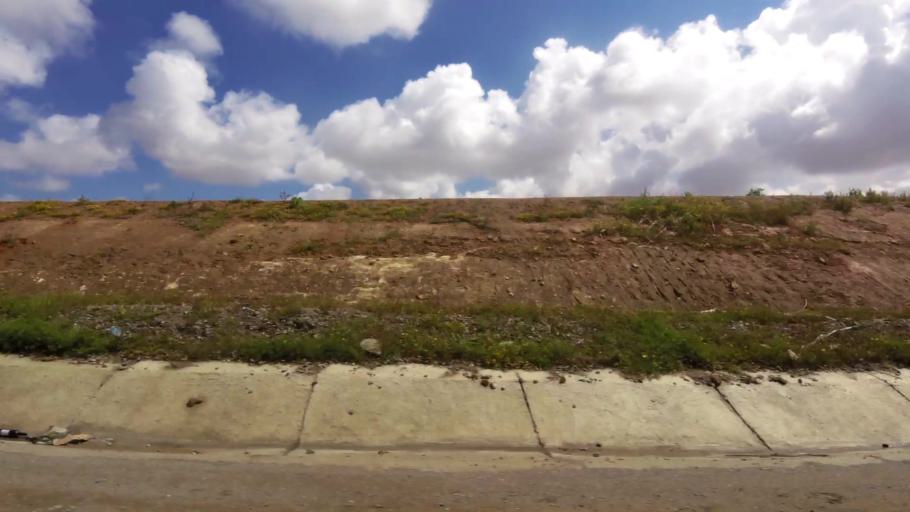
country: MA
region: Grand Casablanca
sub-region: Nouaceur
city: Bouskoura
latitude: 33.5371
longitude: -7.7114
